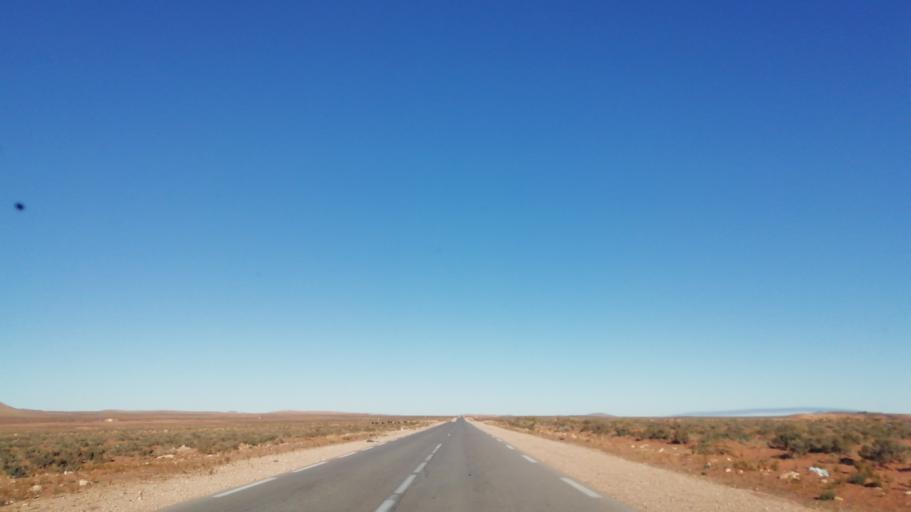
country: DZ
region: El Bayadh
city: El Abiodh Sidi Cheikh
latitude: 33.1150
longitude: 0.2653
